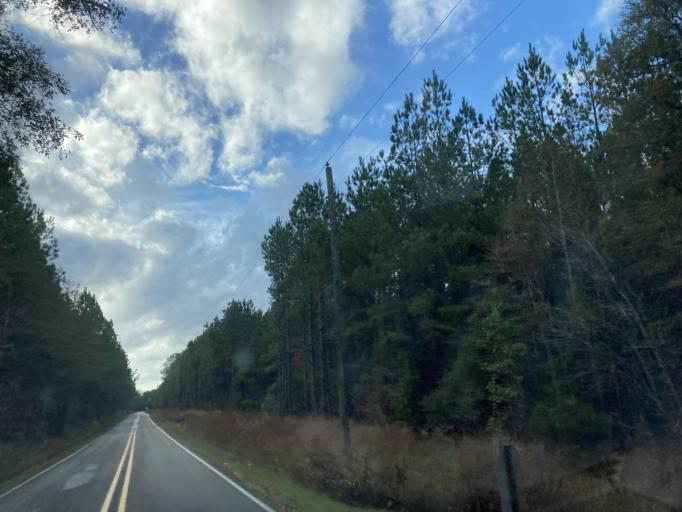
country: US
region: Mississippi
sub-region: Lamar County
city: Purvis
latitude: 31.1629
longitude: -89.5912
